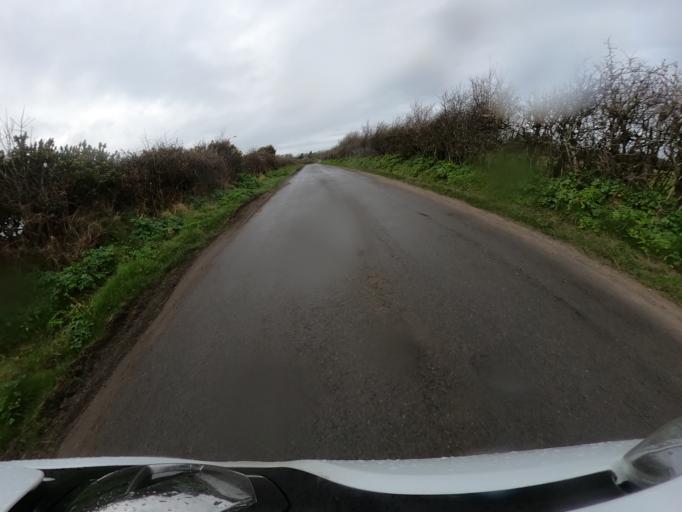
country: IM
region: Ramsey
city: Ramsey
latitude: 54.3806
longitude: -4.4610
